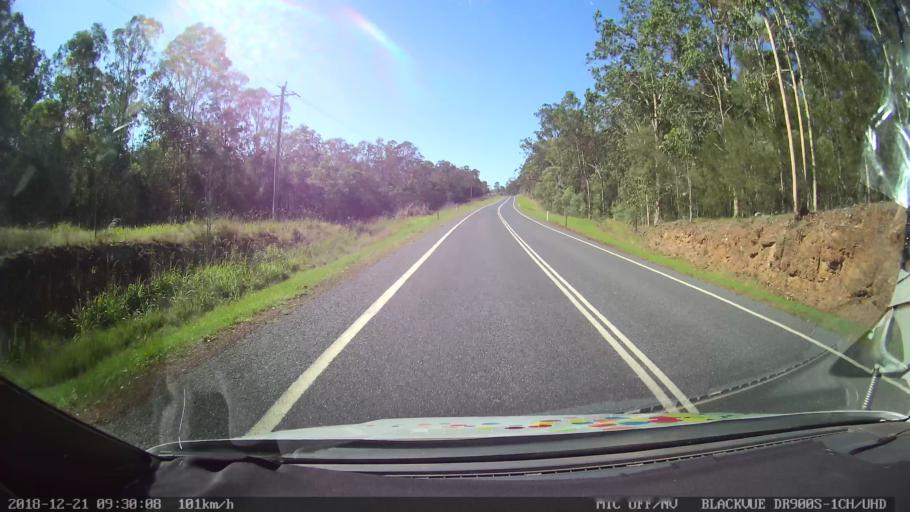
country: AU
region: New South Wales
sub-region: Clarence Valley
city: Maclean
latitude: -29.4421
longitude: 152.9916
